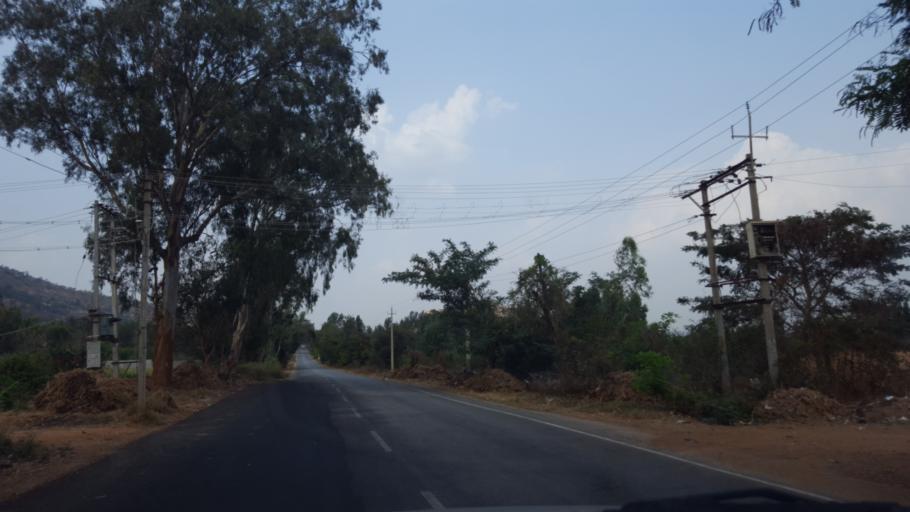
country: IN
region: Karnataka
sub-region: Chikkaballapur
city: Chik Ballapur
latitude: 13.3619
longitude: 77.6934
